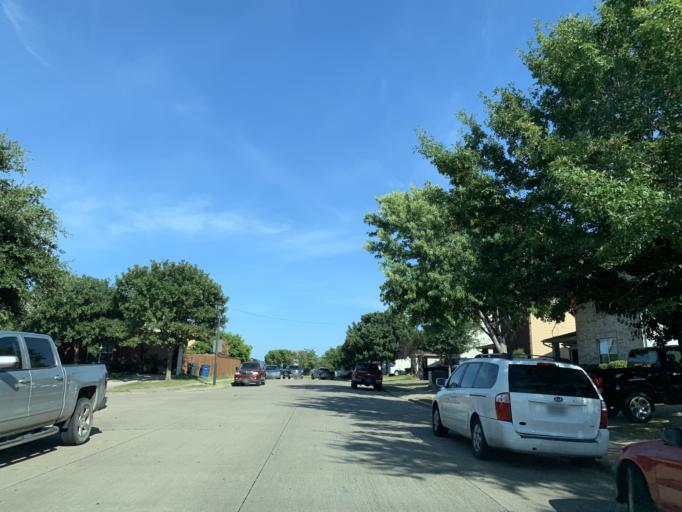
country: US
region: Texas
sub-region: Dallas County
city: Cockrell Hill
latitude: 32.7069
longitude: -96.8973
